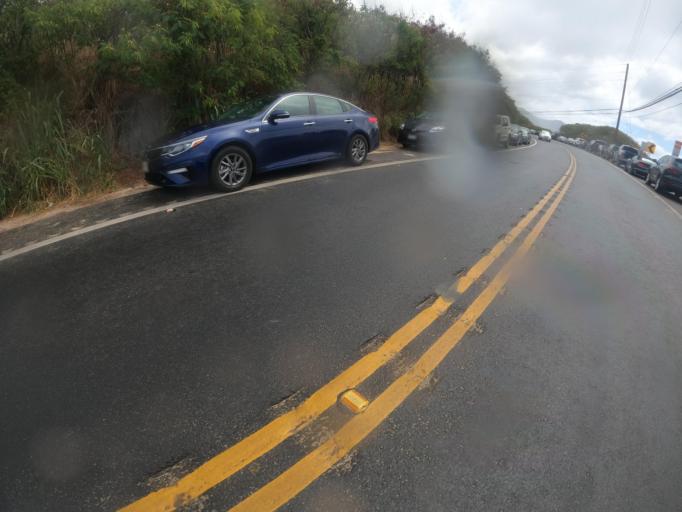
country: US
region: Hawaii
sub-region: Honolulu County
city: Makaha Valley
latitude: 21.5462
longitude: -158.2402
